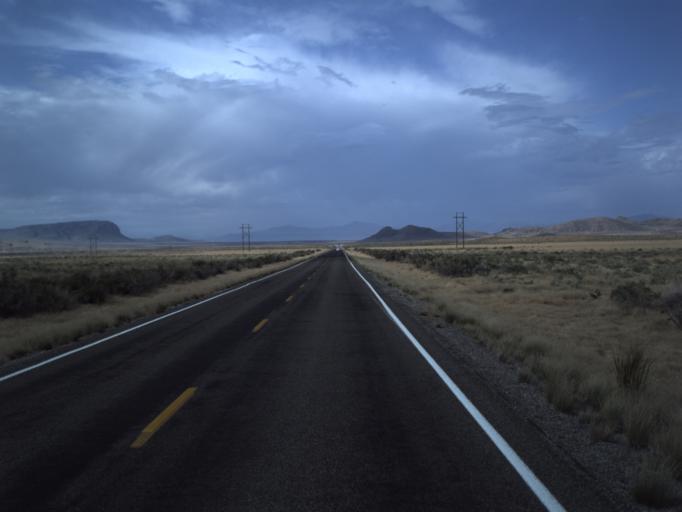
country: US
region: Utah
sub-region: Tooele County
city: Wendover
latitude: 41.4160
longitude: -113.9168
